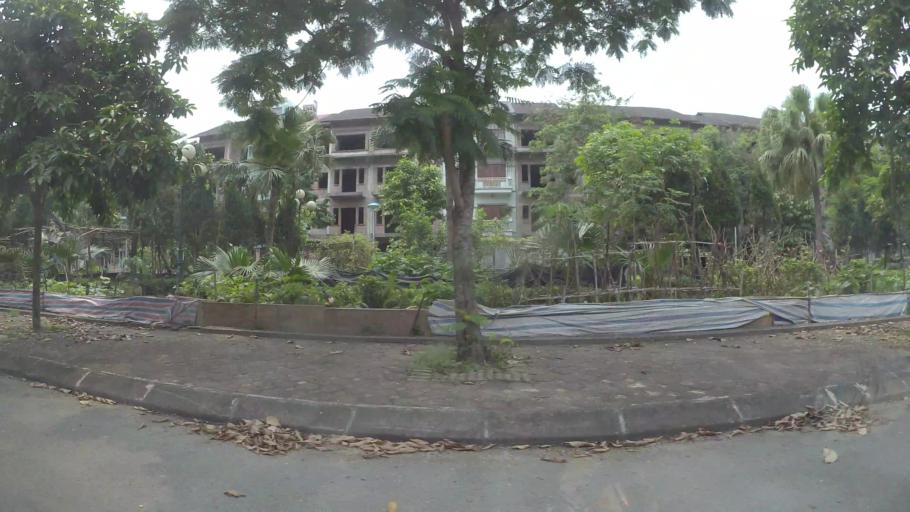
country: VN
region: Ha Noi
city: Cau Dien
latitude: 21.0245
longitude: 105.7451
